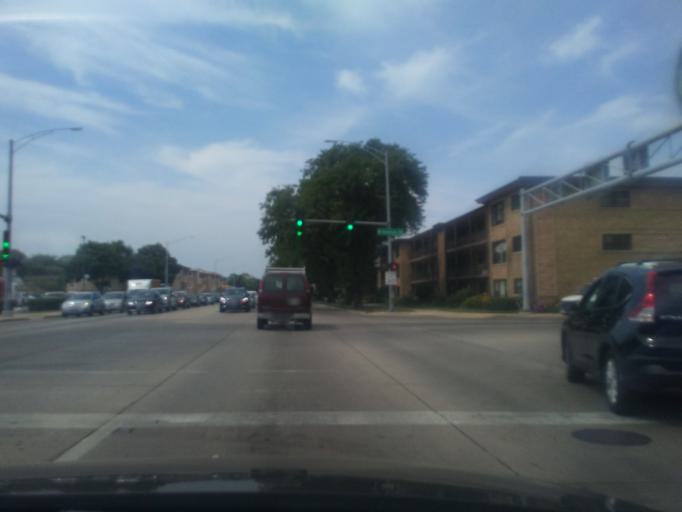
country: US
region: Illinois
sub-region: Cook County
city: Harwood Heights
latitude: 41.9681
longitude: -87.8071
